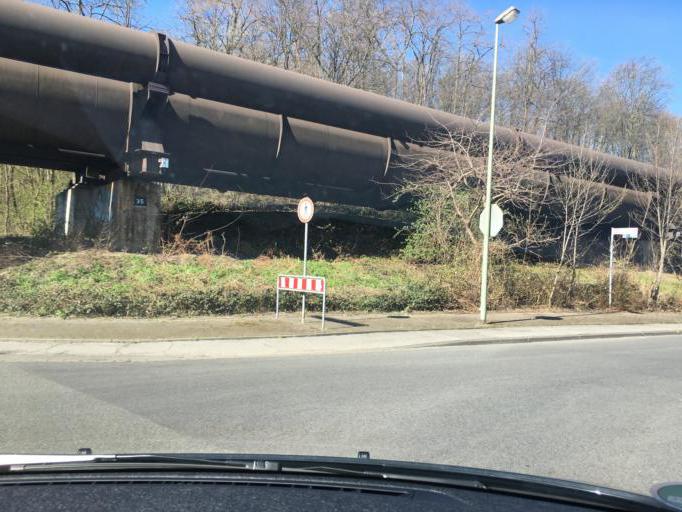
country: DE
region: North Rhine-Westphalia
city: Meiderich
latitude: 51.4971
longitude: 6.7288
